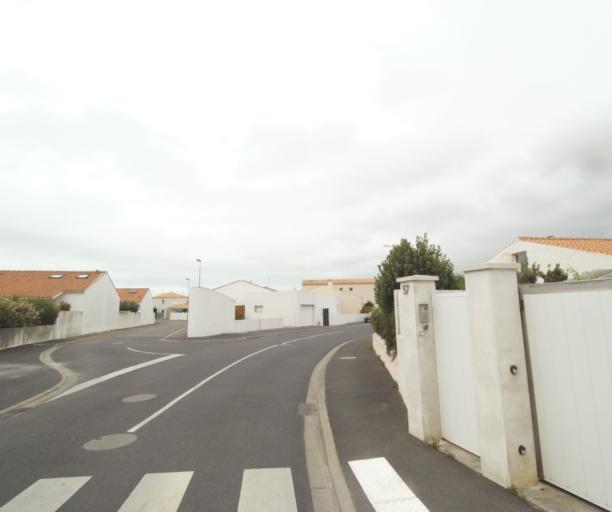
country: FR
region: Pays de la Loire
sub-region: Departement de la Vendee
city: Chateau-d'Olonne
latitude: 46.4877
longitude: -1.7552
